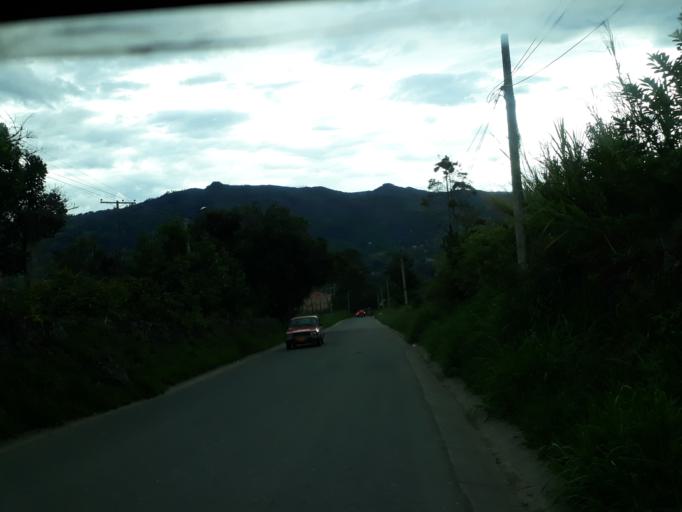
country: CO
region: Cundinamarca
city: Pacho
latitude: 5.1523
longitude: -74.1483
